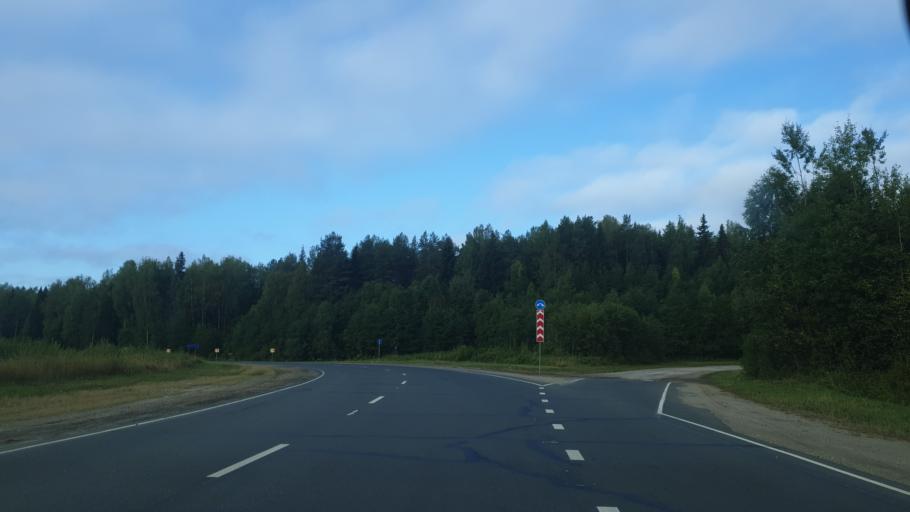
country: RU
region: Komi Republic
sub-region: Syktyvdinskiy Rayon
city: Syktyvkar
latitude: 61.5596
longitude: 50.6346
